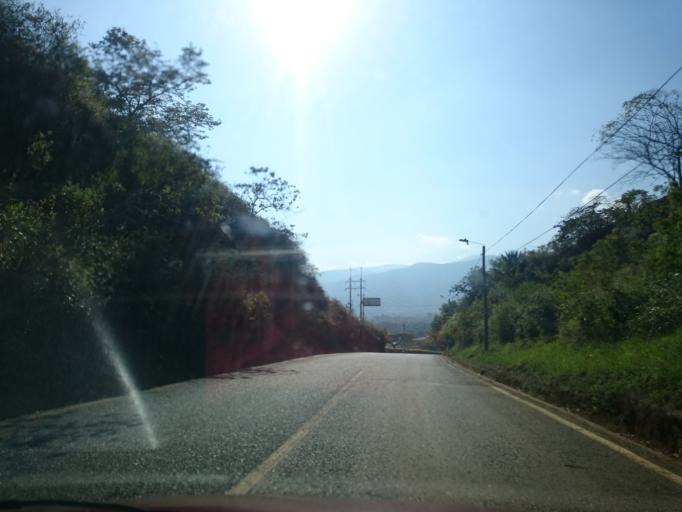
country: CO
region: Cauca
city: Caloto
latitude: 3.0385
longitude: -76.4127
